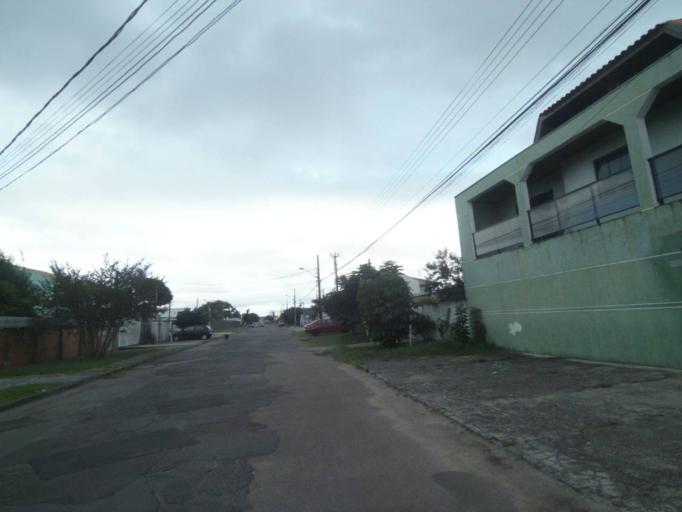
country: BR
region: Parana
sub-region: Pinhais
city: Pinhais
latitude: -25.4606
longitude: -49.2055
